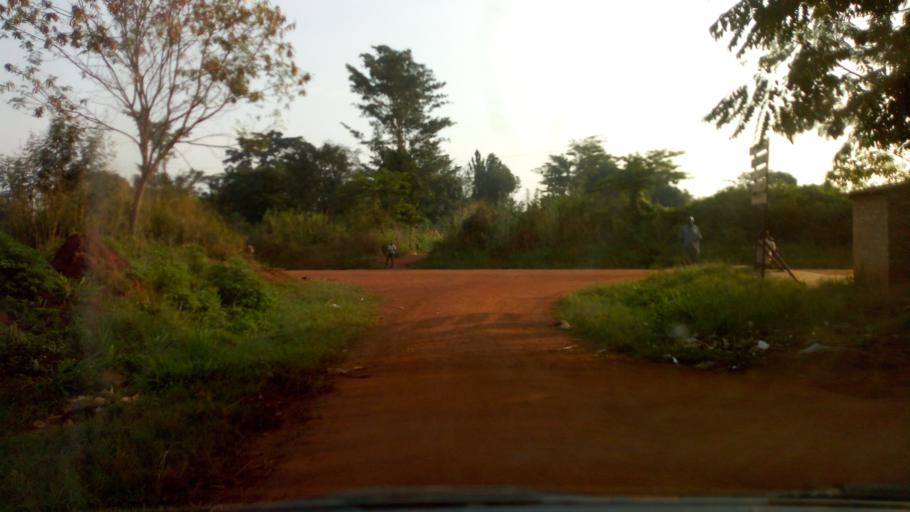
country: UG
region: Western Region
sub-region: Masindi District
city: Masindi
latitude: 1.7735
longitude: 31.8395
